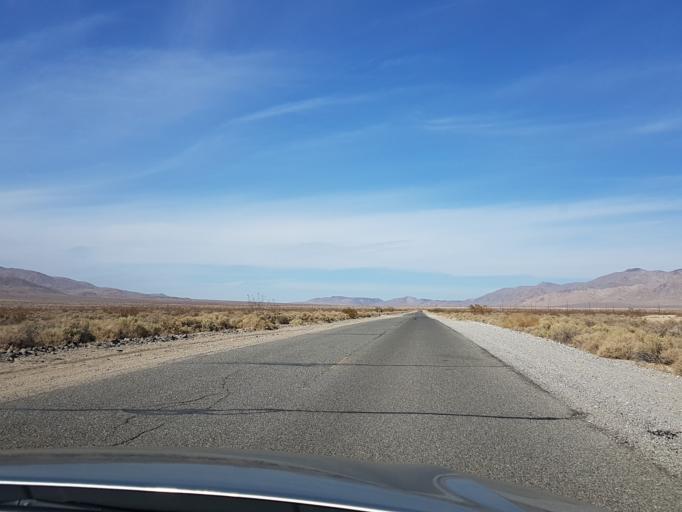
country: US
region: California
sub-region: San Bernardino County
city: Searles Valley
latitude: 35.8231
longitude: -117.3404
